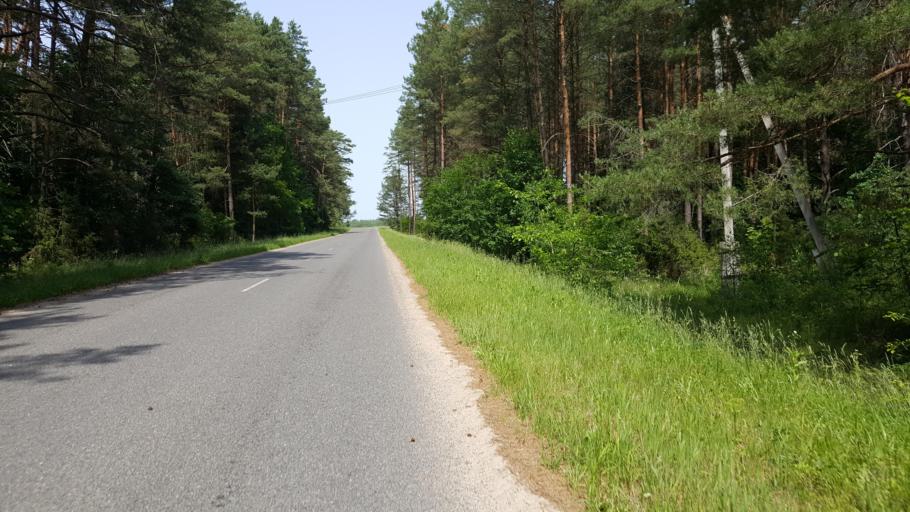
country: BY
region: Brest
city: Kamyanyuki
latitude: 52.5129
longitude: 23.8526
